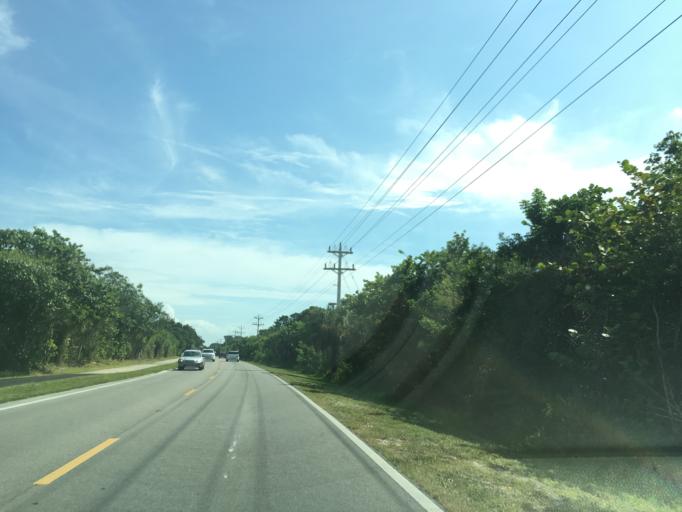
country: US
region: Florida
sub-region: Lee County
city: Saint James City
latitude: 26.4404
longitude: -82.1012
